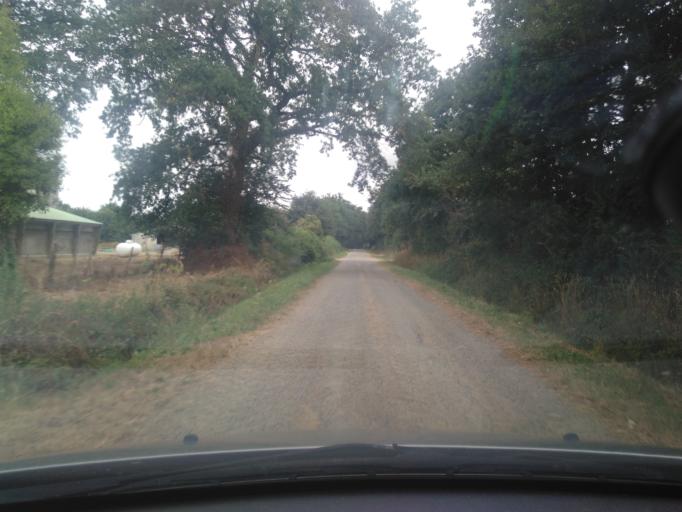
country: FR
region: Pays de la Loire
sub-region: Departement de la Vendee
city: La Ferriere
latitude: 46.7101
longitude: -1.2977
